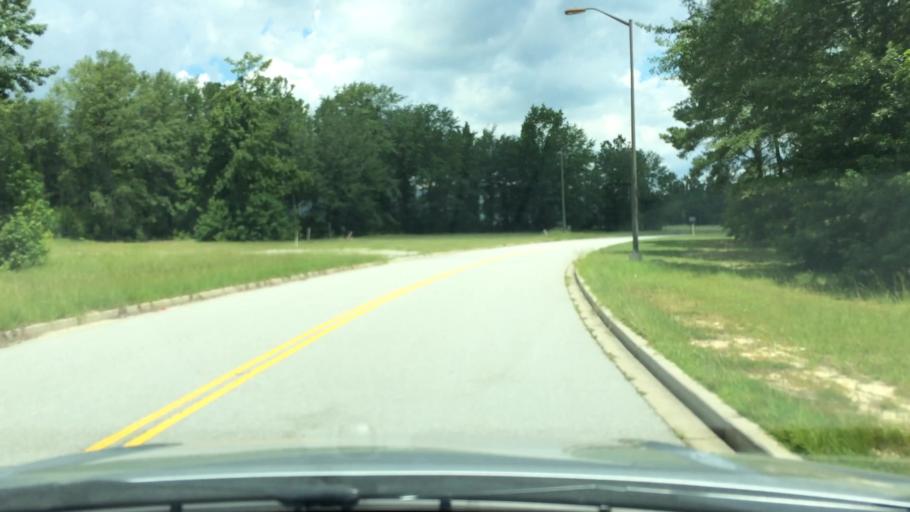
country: US
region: South Carolina
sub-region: Calhoun County
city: Oak Grove
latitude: 33.8013
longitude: -81.0055
